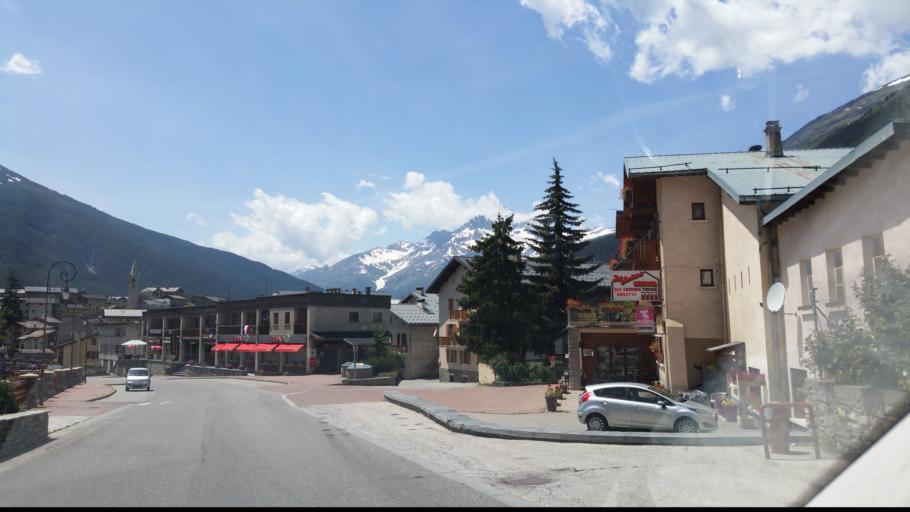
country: IT
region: Piedmont
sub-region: Provincia di Torino
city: Moncenisio
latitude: 45.2914
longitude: 6.9157
